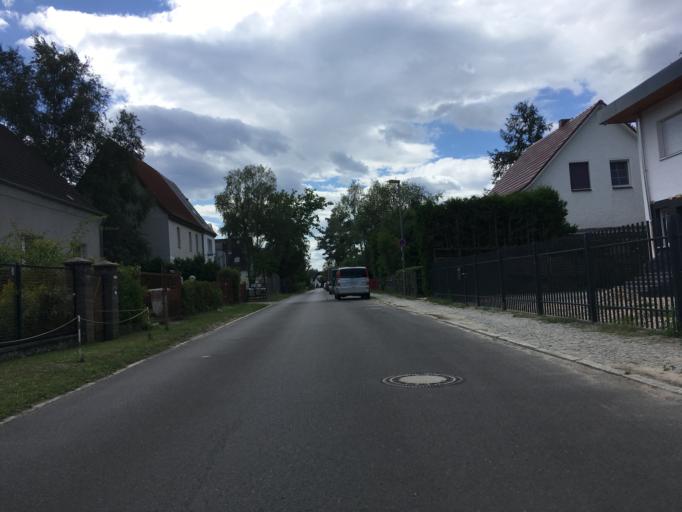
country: DE
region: Berlin
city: Staaken
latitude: 52.5480
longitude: 13.1289
